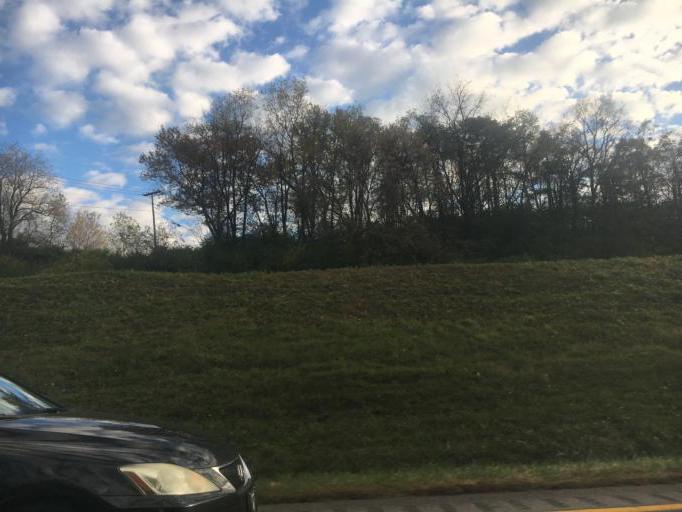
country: US
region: Virginia
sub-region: Washington County
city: Abingdon
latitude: 36.6995
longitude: -81.9819
